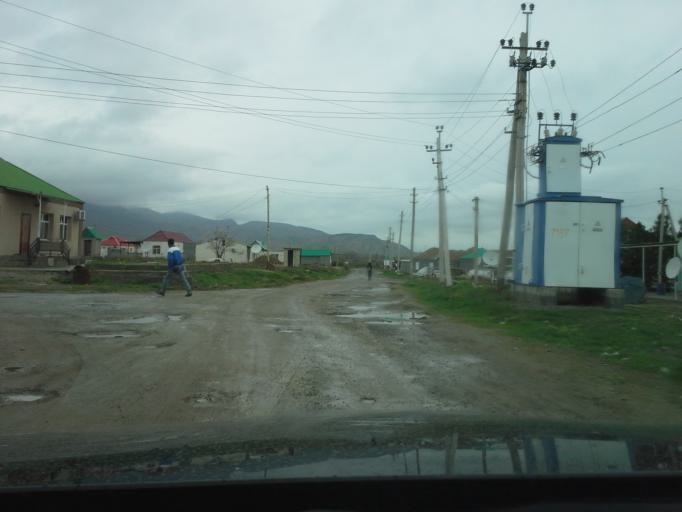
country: TM
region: Ahal
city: Abadan
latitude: 37.9602
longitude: 58.2024
